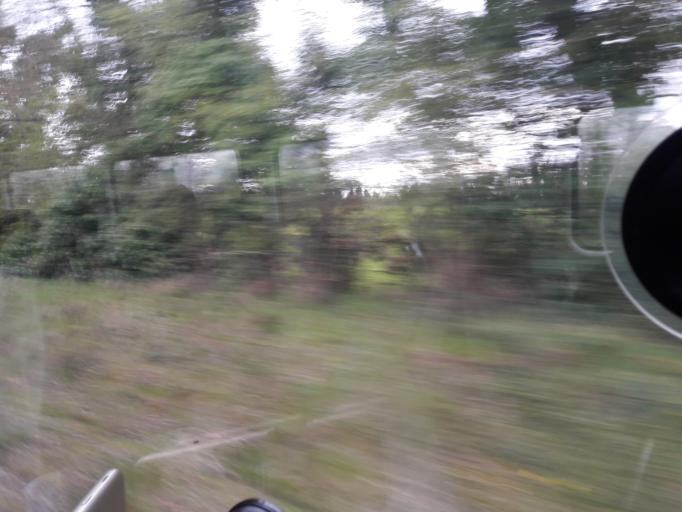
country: IE
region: Leinster
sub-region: An Iarmhi
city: An Muileann gCearr
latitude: 53.5425
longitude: -7.3493
